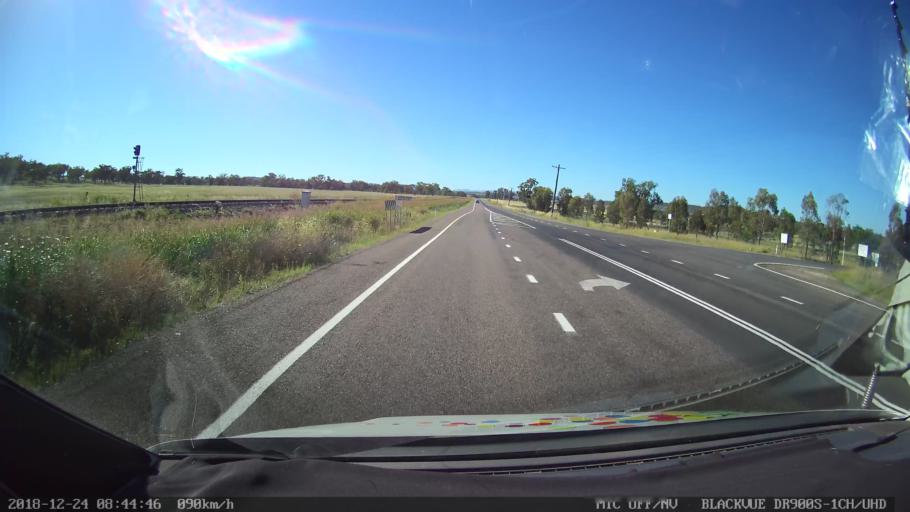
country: AU
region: New South Wales
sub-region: Liverpool Plains
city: Quirindi
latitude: -31.4060
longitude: 150.6495
